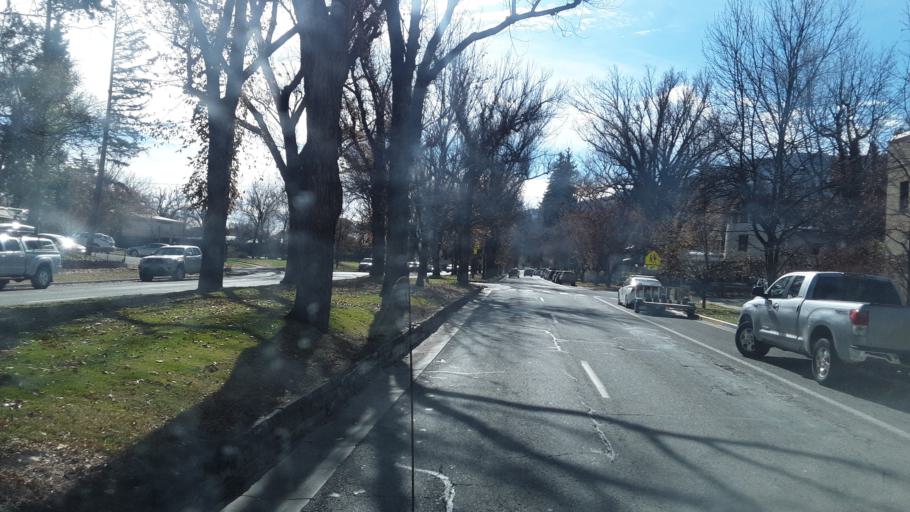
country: US
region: Colorado
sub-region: La Plata County
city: Durango
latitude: 37.2777
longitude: -107.8764
